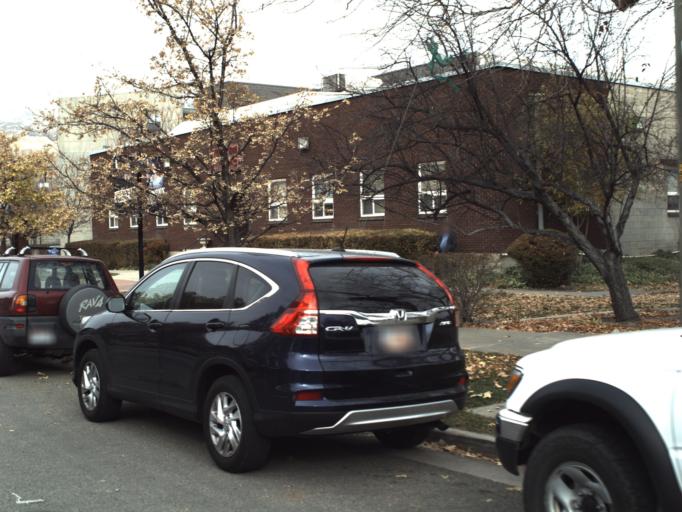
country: US
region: Utah
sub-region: Salt Lake County
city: Salt Lake City
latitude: 40.7764
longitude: -111.9024
